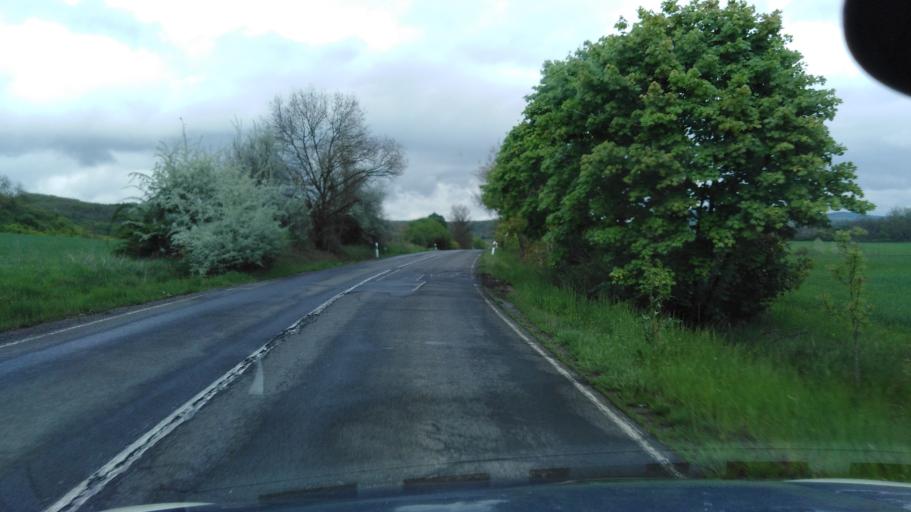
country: HU
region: Nograd
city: Szecseny
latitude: 48.1203
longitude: 19.5496
